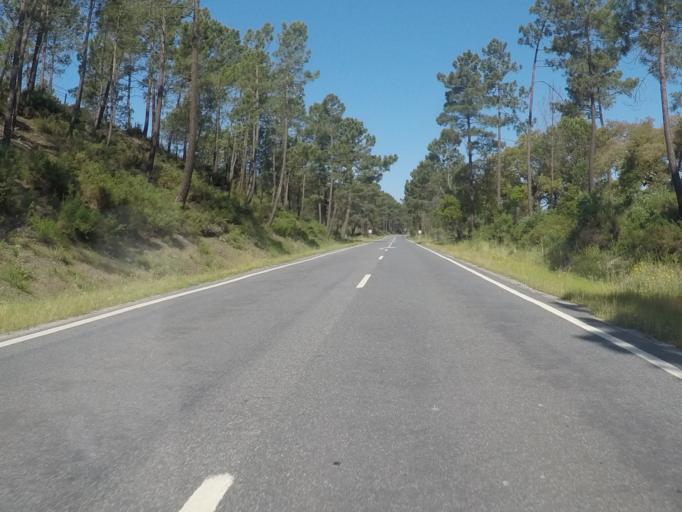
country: PT
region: Setubal
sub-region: Grandola
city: Grandola
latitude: 38.3005
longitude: -8.7303
